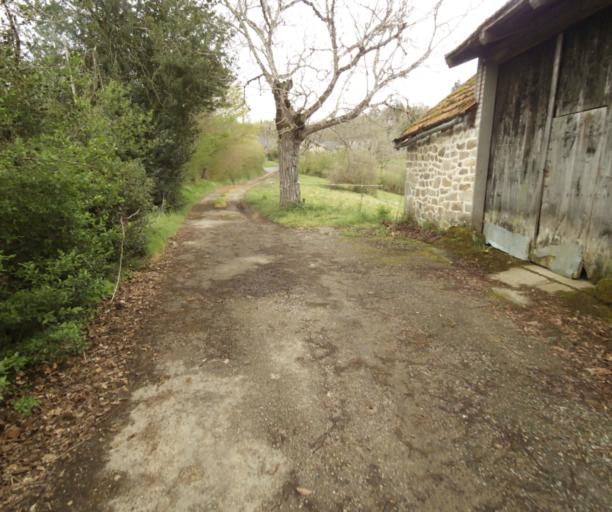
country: FR
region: Limousin
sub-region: Departement de la Correze
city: Naves
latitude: 45.2901
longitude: 1.7966
